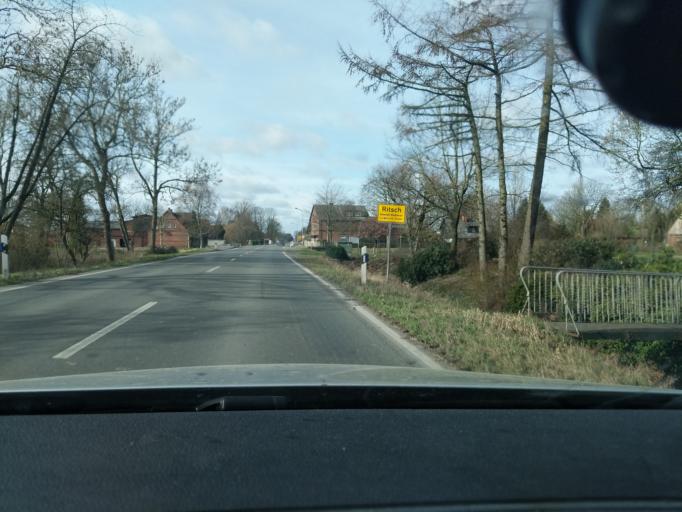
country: DE
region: Lower Saxony
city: Drochtersen
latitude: 53.6966
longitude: 9.4176
